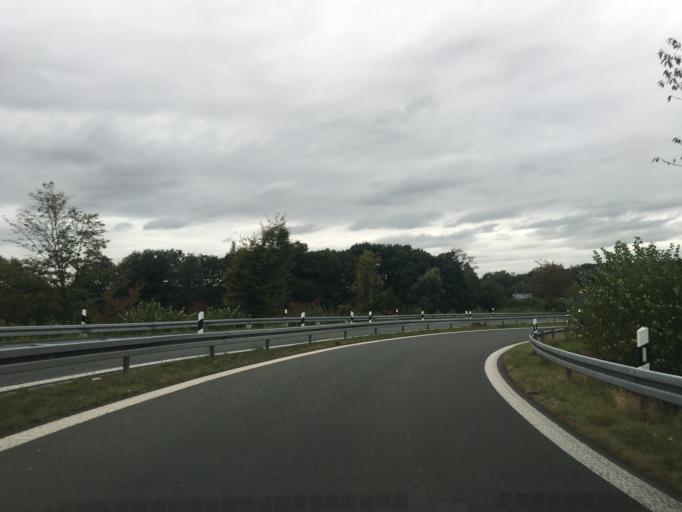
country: DE
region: North Rhine-Westphalia
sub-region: Regierungsbezirk Munster
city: Ochtrup
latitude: 52.1912
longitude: 7.1178
